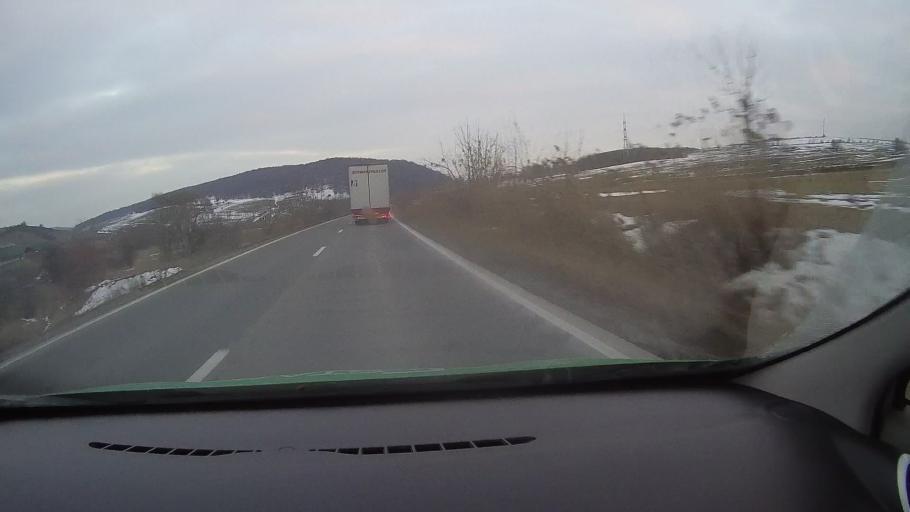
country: RO
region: Harghita
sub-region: Municipiul Odorheiu Secuiesc
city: Odorheiu Secuiesc
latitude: 46.3446
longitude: 25.2663
